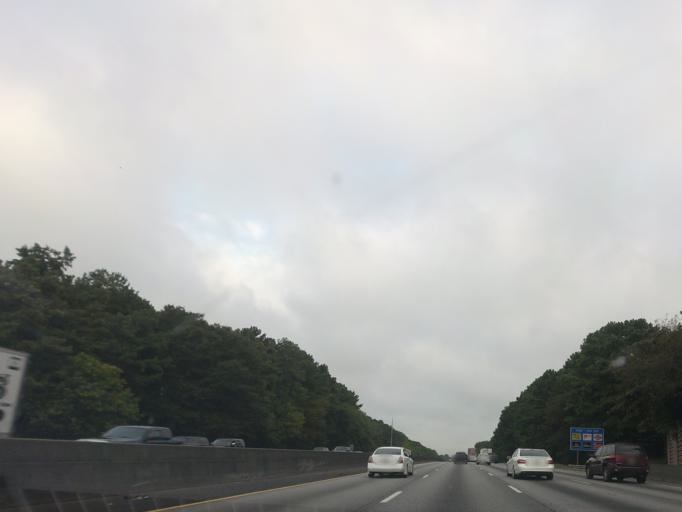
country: US
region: Georgia
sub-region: Clayton County
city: Morrow
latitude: 33.5806
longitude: -84.3588
